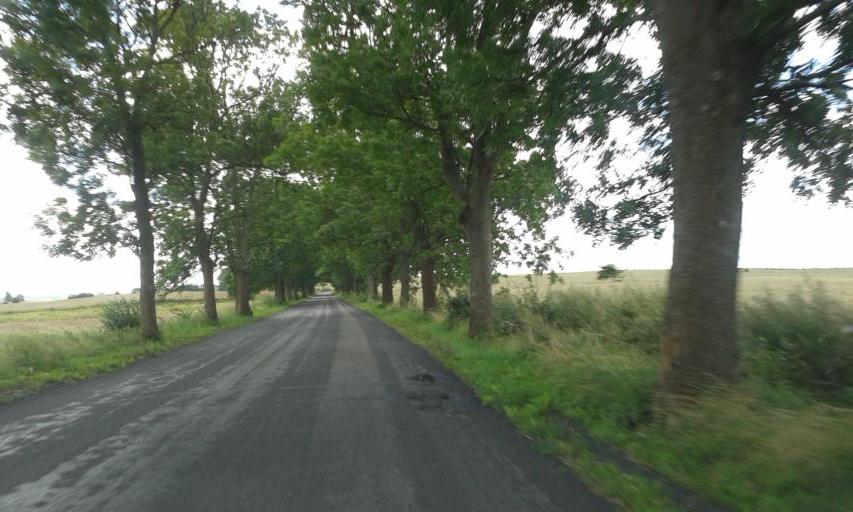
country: PL
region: West Pomeranian Voivodeship
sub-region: Powiat walecki
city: Walcz
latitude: 53.2277
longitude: 16.5446
